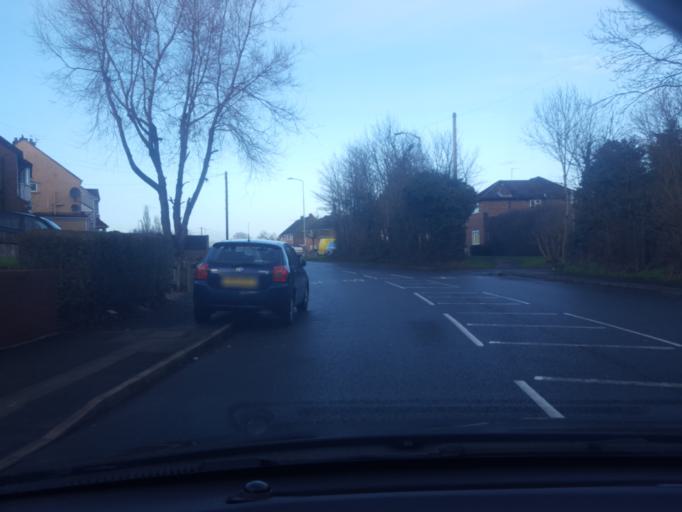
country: GB
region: England
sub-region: Wolverhampton
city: Wolverhampton
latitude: 52.6080
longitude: -2.1508
